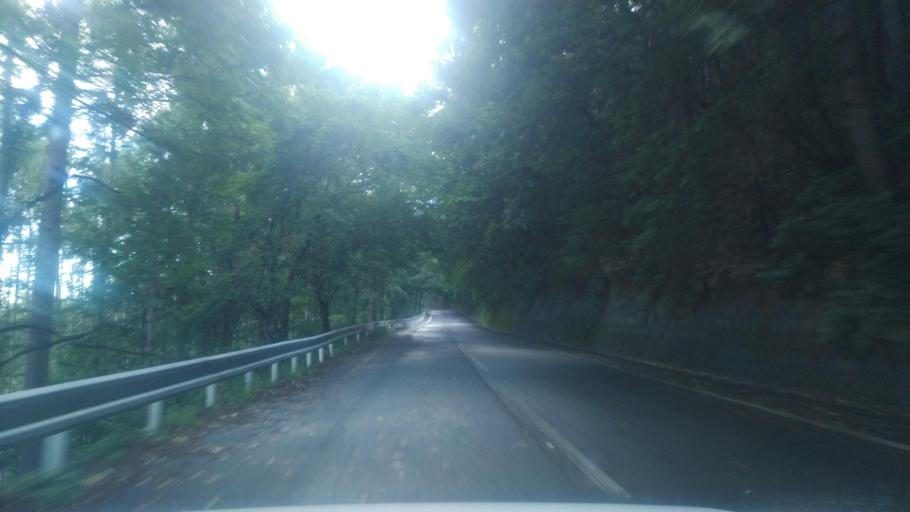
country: JP
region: Nagano
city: Ueda
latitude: 36.5158
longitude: 138.3654
